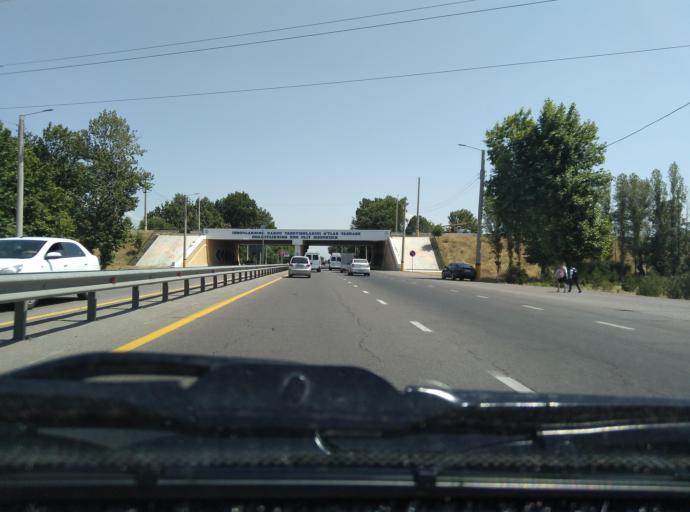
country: UZ
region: Toshkent Shahri
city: Bektemir
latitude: 41.2455
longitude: 69.3949
